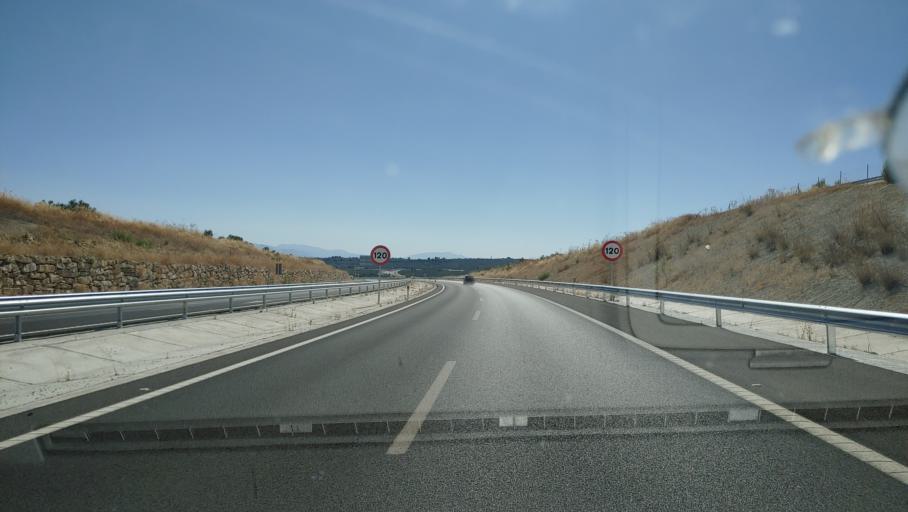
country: ES
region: Andalusia
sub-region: Provincia de Jaen
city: Sabiote
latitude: 38.0494
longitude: -3.3063
